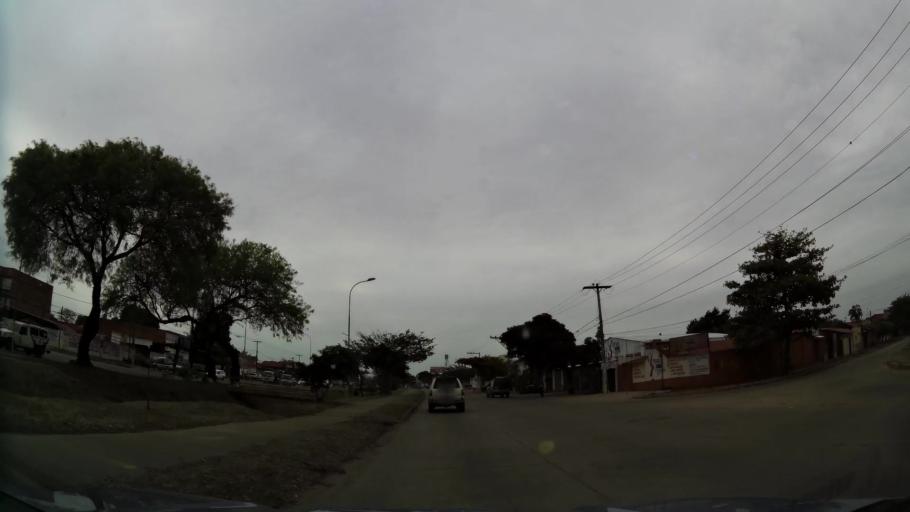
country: BO
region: Santa Cruz
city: Santa Cruz de la Sierra
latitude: -17.8090
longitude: -63.1575
